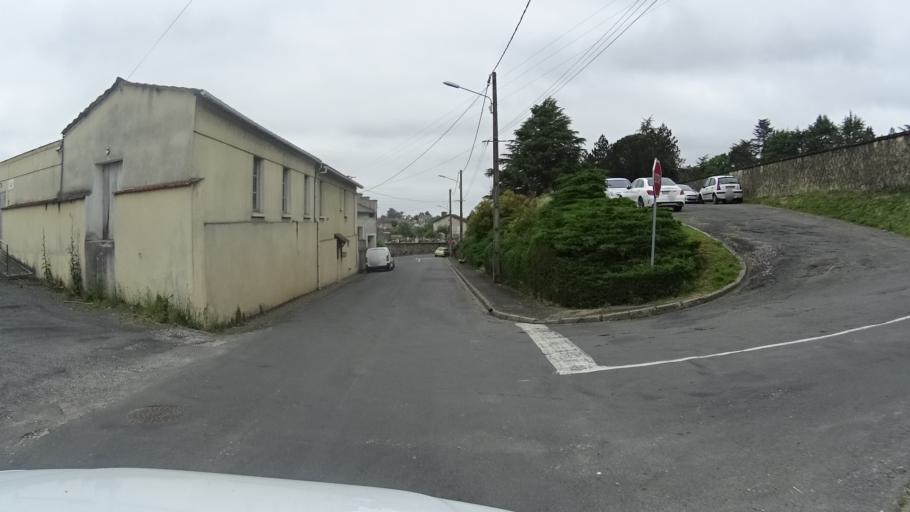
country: FR
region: Aquitaine
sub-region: Departement de la Dordogne
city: Mussidan
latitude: 45.0338
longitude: 0.3724
